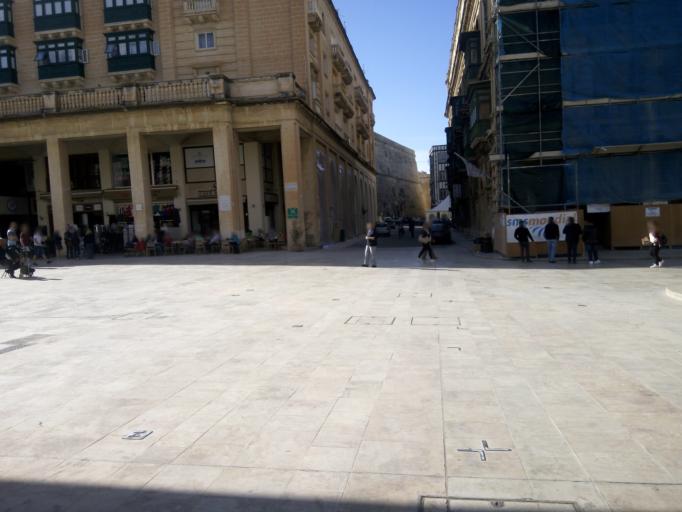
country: MT
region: Il-Furjana
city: Floriana
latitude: 35.8964
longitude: 14.5101
